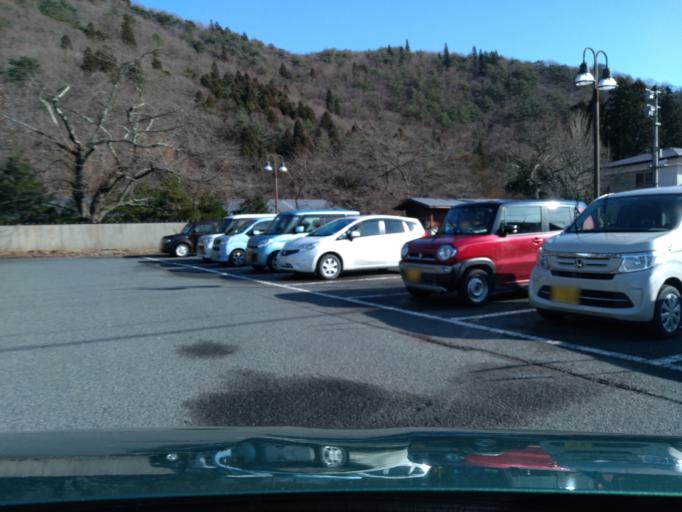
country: JP
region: Iwate
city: Hanamaki
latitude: 39.4354
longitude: 141.0154
